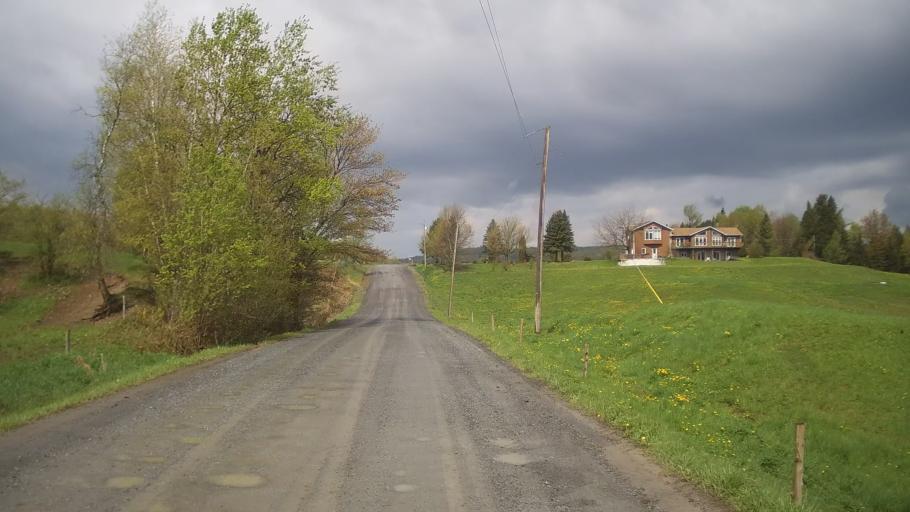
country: CA
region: Quebec
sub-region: Monteregie
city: Cowansville
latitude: 45.1737
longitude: -72.6751
